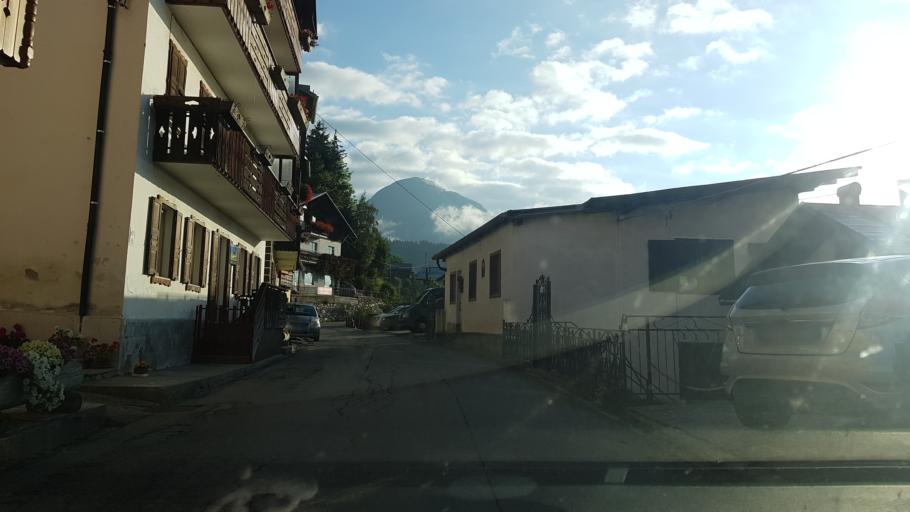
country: IT
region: Veneto
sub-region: Provincia di Belluno
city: San Pietro di Cadore
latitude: 46.5798
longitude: 12.5743
